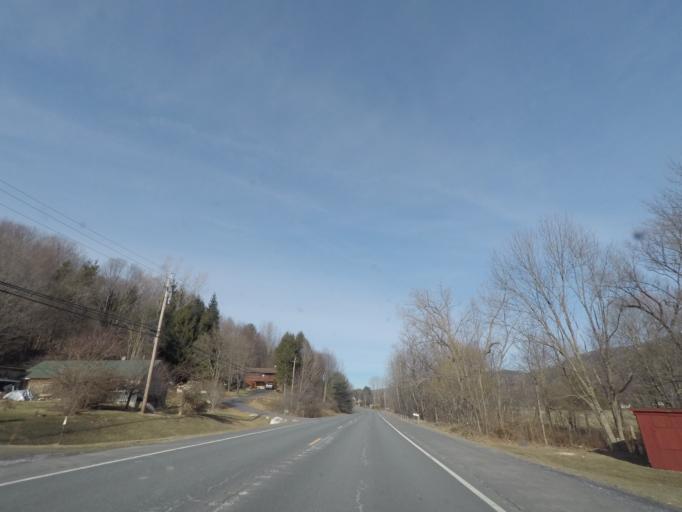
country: US
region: Massachusetts
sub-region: Berkshire County
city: Williamstown
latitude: 42.7162
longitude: -73.3745
